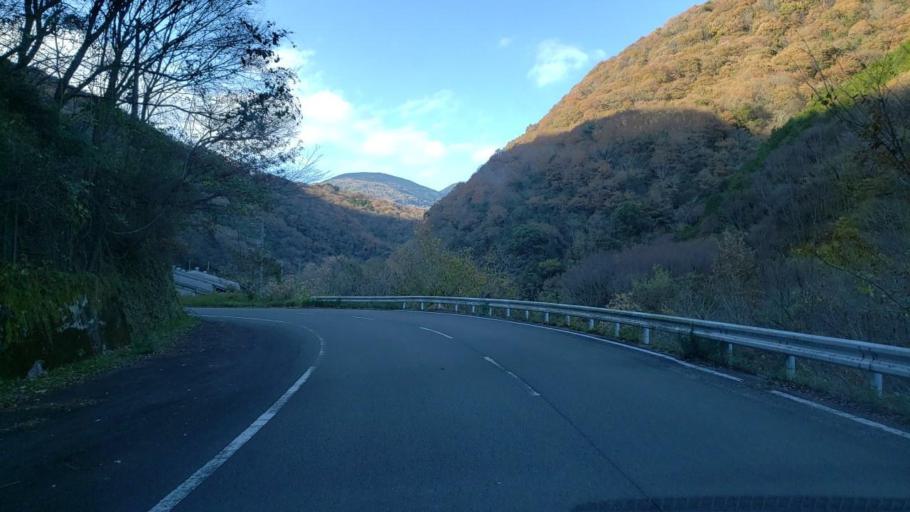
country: JP
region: Tokushima
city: Wakimachi
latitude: 34.0767
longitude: 134.0766
